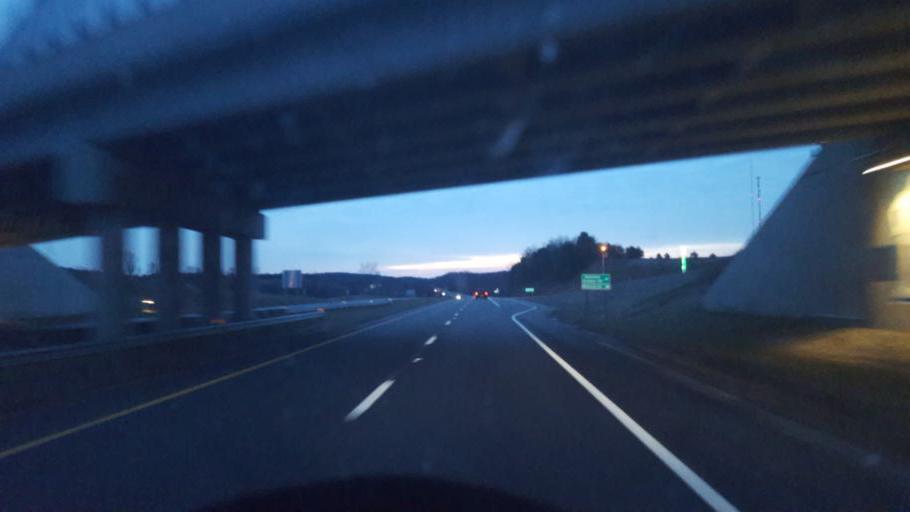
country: US
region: Ohio
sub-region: Jackson County
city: Jackson
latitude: 39.0366
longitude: -82.6019
